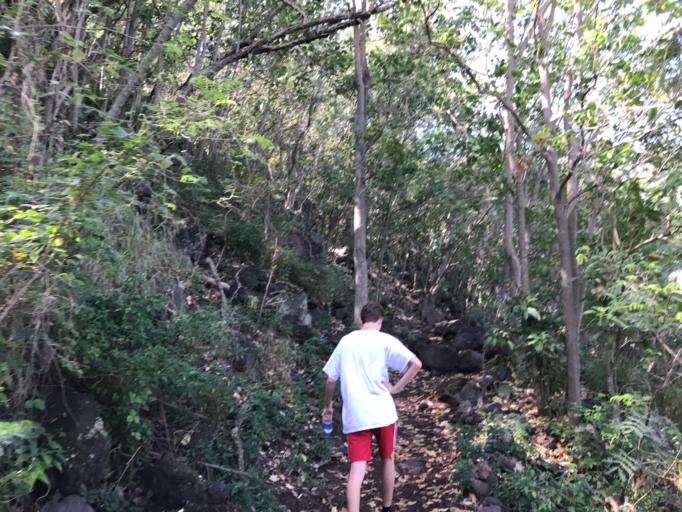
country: US
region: Hawaii
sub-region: Honolulu County
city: Mokuleia
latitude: 21.5737
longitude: -158.2082
